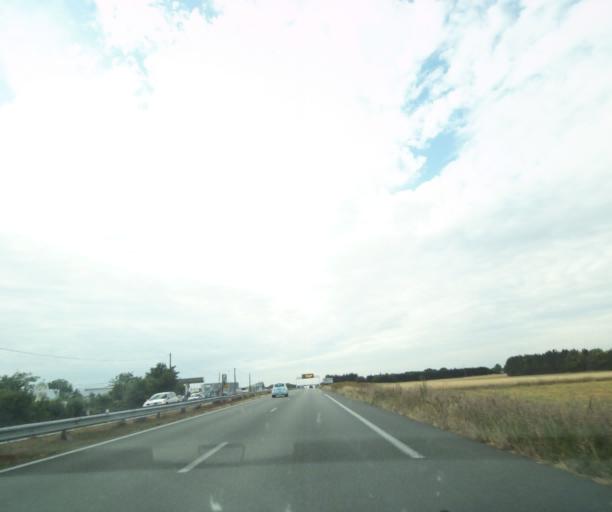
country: FR
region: Poitou-Charentes
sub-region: Departement de la Charente-Maritime
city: Angoulins
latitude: 46.0988
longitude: -1.0912
